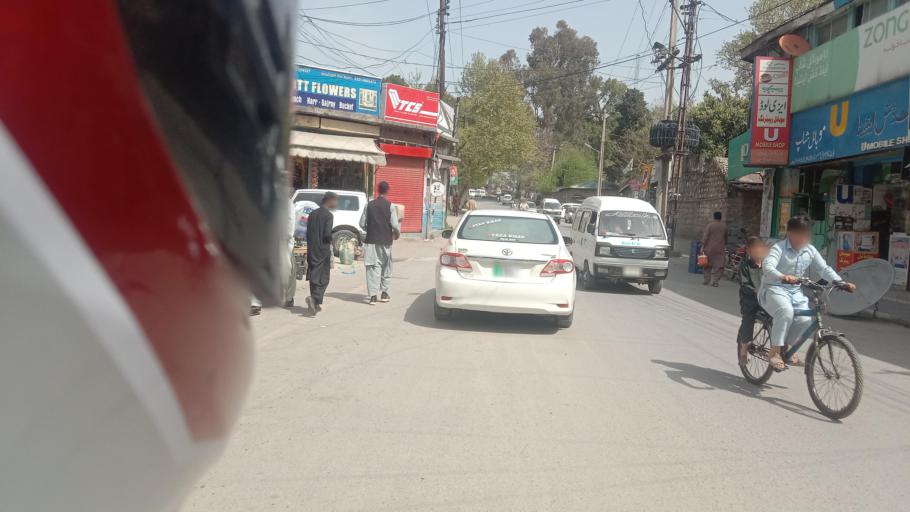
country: PK
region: Khyber Pakhtunkhwa
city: Abbottabad
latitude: 34.1478
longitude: 73.2131
